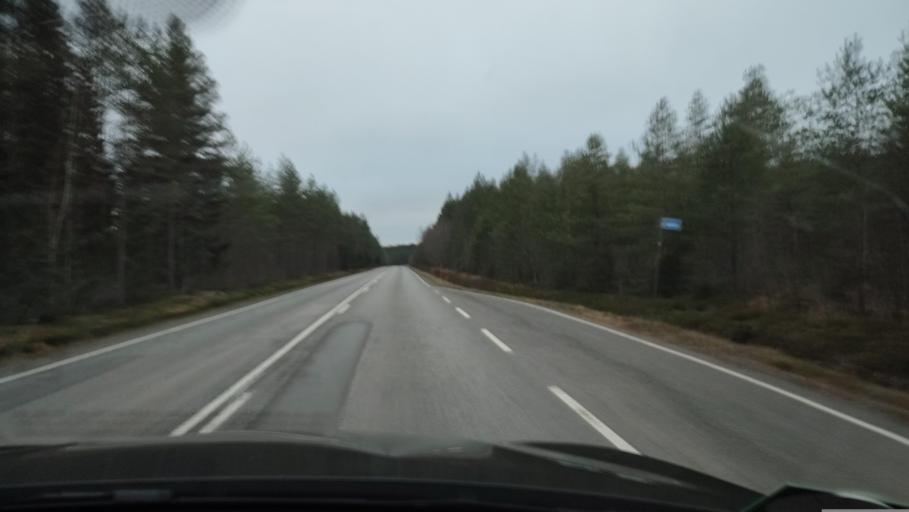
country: FI
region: Southern Ostrobothnia
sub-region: Suupohja
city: Karijoki
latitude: 62.3225
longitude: 21.7973
